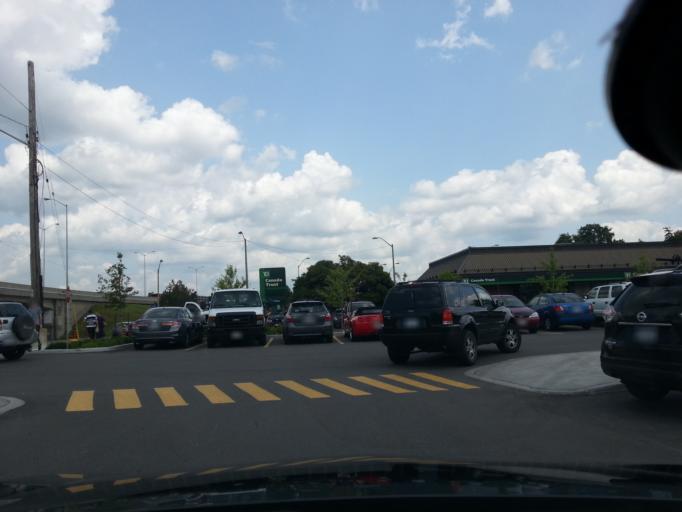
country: CA
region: Ontario
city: Ottawa
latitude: 45.4110
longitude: -75.6854
